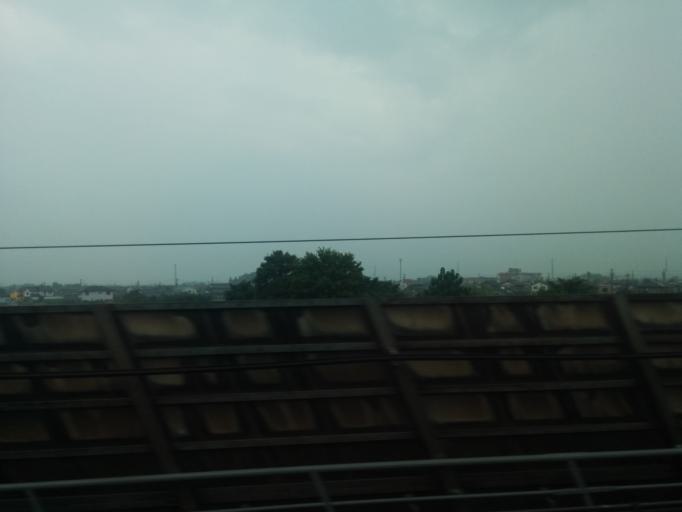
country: JP
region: Aichi
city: Sobue
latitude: 35.2793
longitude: 136.7484
